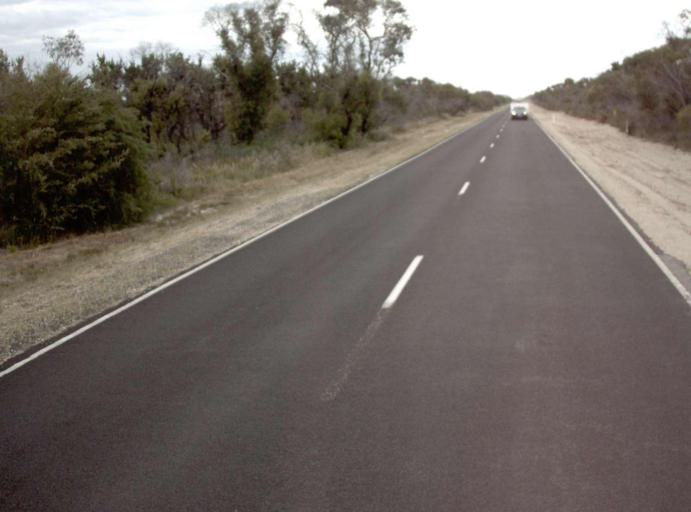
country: AU
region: Victoria
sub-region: East Gippsland
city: Bairnsdale
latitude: -38.1105
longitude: 147.4698
